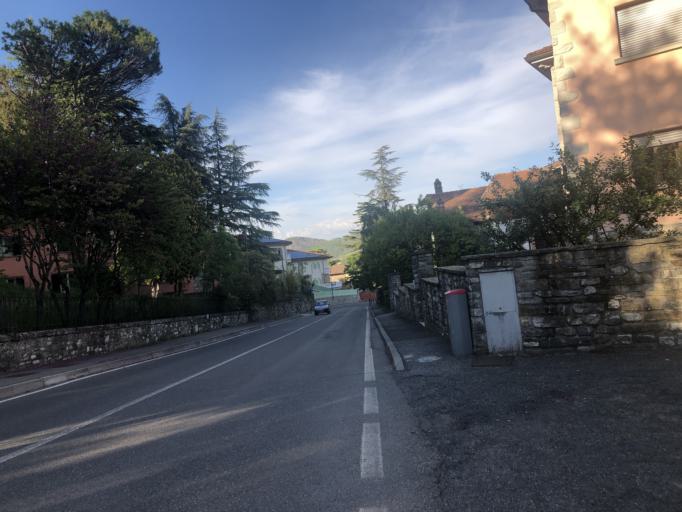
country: IT
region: Emilia-Romagna
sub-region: Provincia di Piacenza
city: Bobbio
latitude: 44.7696
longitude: 9.3841
